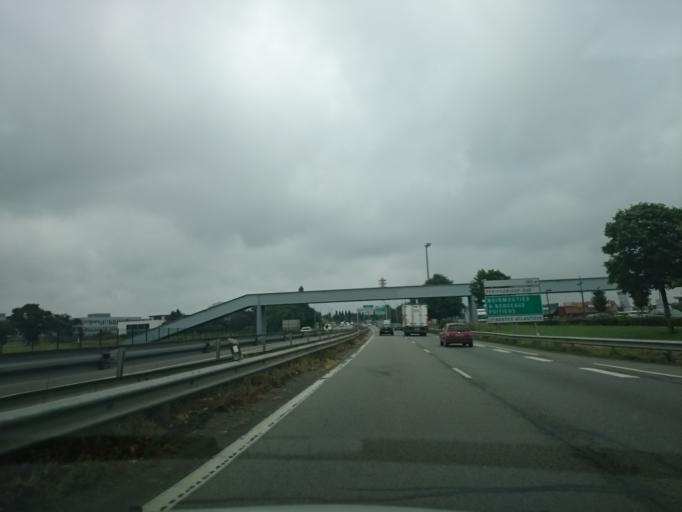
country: FR
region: Pays de la Loire
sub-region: Departement de la Loire-Atlantique
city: Saint-Herblain
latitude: 47.2267
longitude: -1.6298
